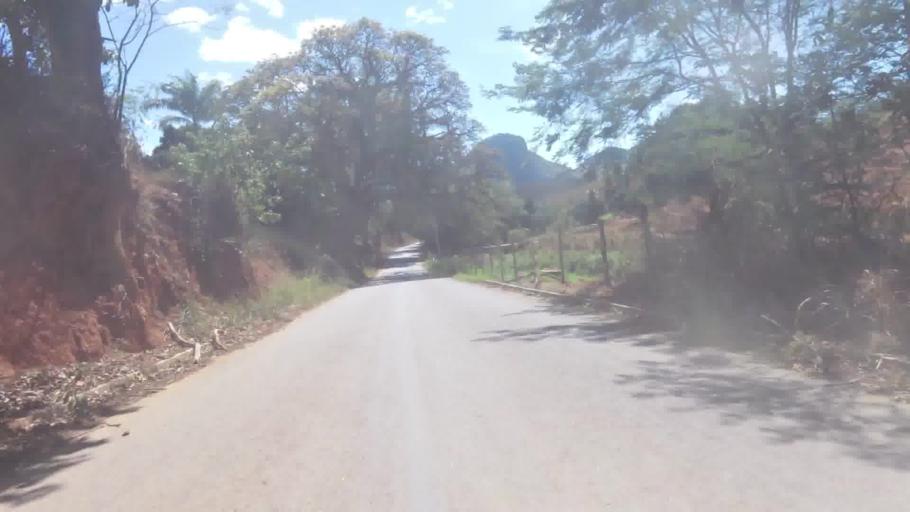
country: BR
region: Espirito Santo
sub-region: Cachoeiro De Itapemirim
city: Cachoeiro de Itapemirim
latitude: -20.9293
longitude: -41.2131
